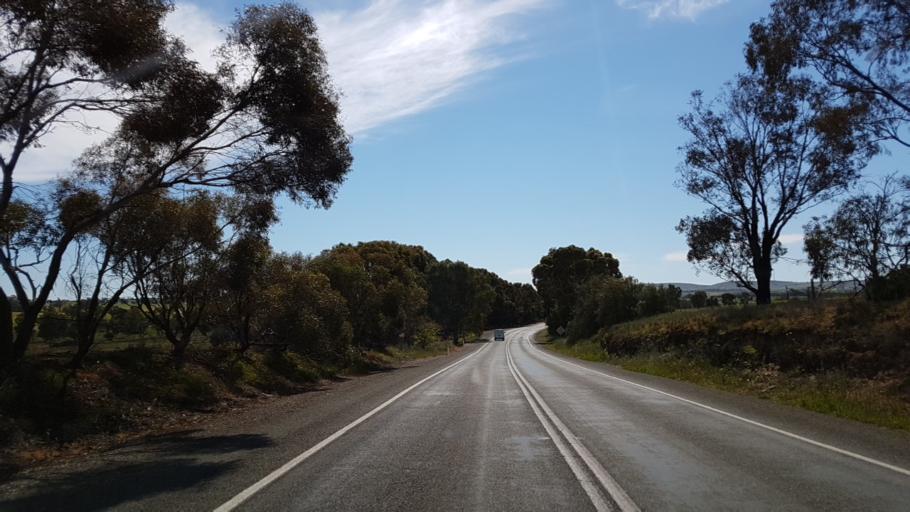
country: AU
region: South Australia
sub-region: Light
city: Freeling
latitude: -34.3592
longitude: 138.7673
